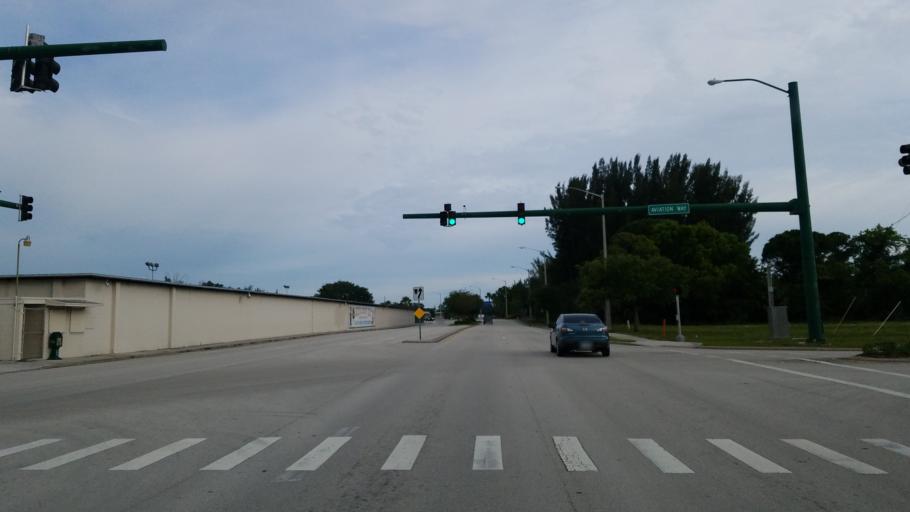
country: US
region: Florida
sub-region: Martin County
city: Sewall's Point
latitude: 27.1715
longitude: -80.2252
